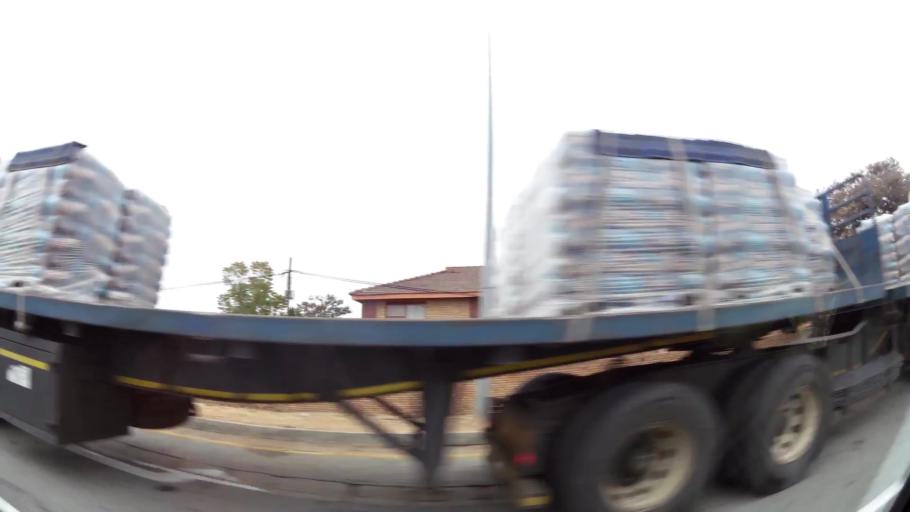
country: ZA
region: Limpopo
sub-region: Capricorn District Municipality
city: Polokwane
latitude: -23.9194
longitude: 29.4393
